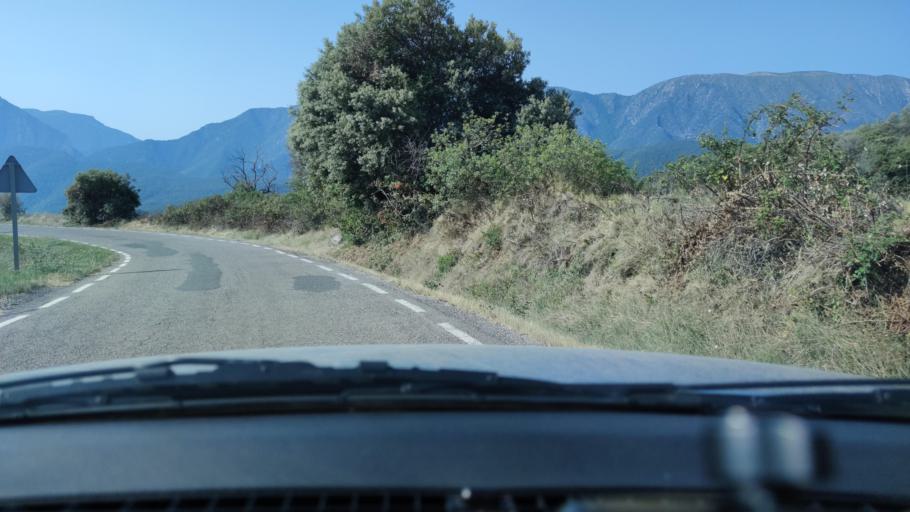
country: ES
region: Catalonia
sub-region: Provincia de Lleida
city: Llimiana
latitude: 42.0860
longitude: 0.8664
